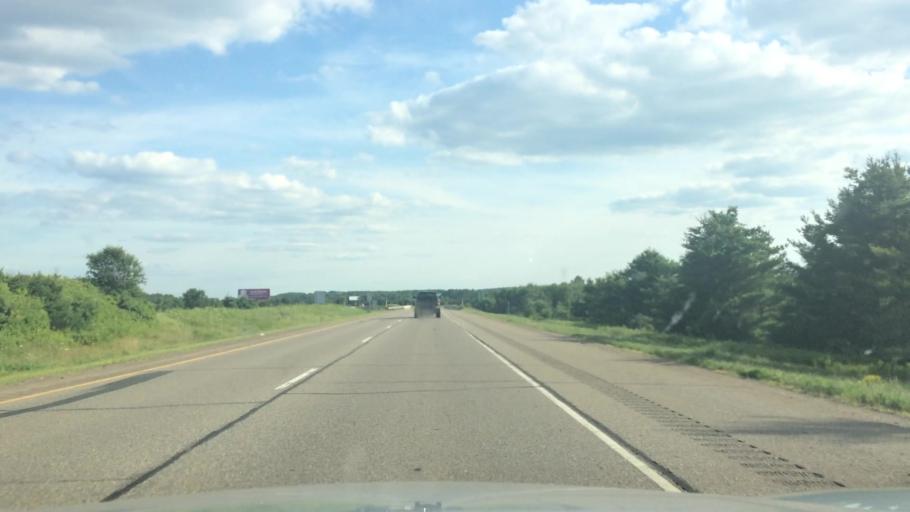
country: US
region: Wisconsin
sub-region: Lincoln County
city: Merrill
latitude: 45.1601
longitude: -89.6436
